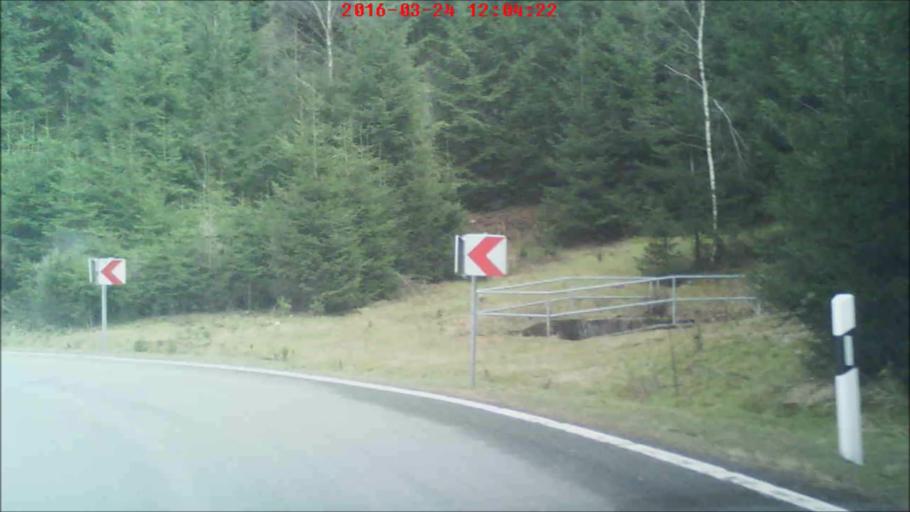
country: DE
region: Thuringia
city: Goldisthal
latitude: 50.5171
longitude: 11.0061
